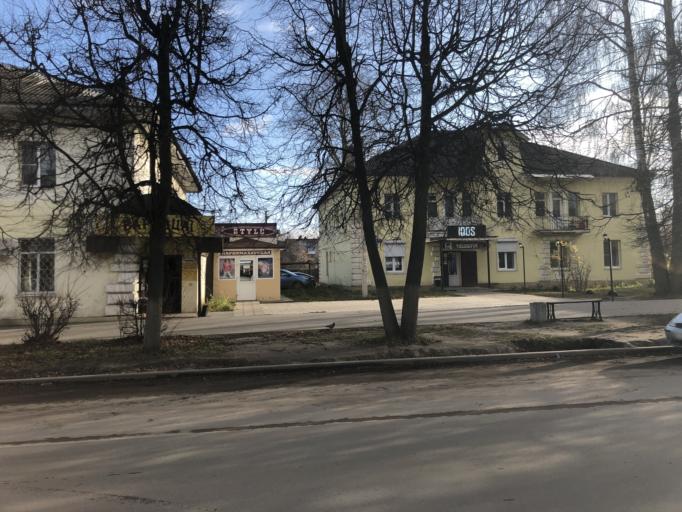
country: RU
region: Tverskaya
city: Rzhev
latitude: 56.2492
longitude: 34.3273
